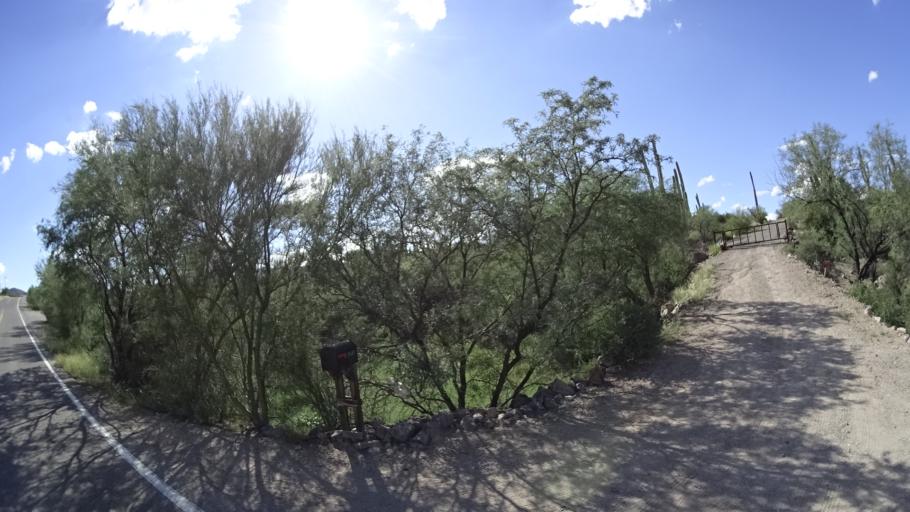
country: US
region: Arizona
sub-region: Pima County
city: Flowing Wells
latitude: 32.2526
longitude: -111.0617
